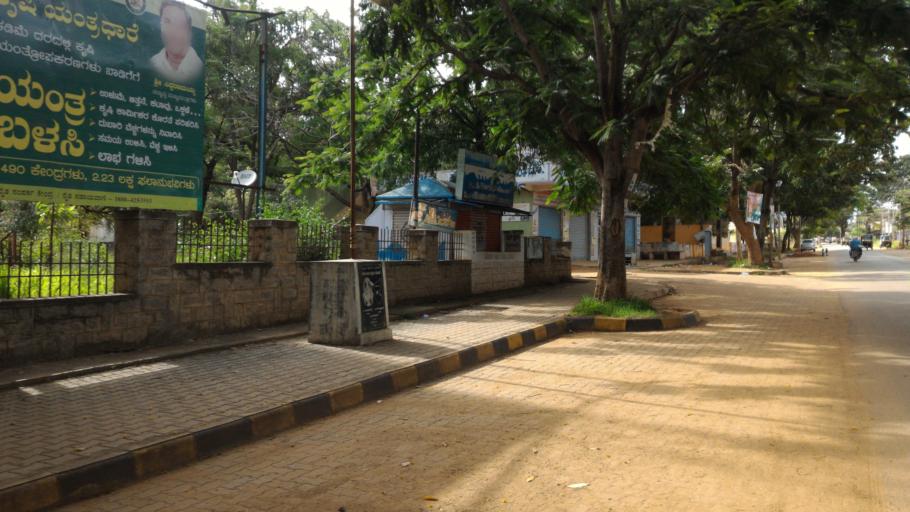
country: IN
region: Karnataka
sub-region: Tumkur
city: Gubbi
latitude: 13.3148
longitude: 76.9406
